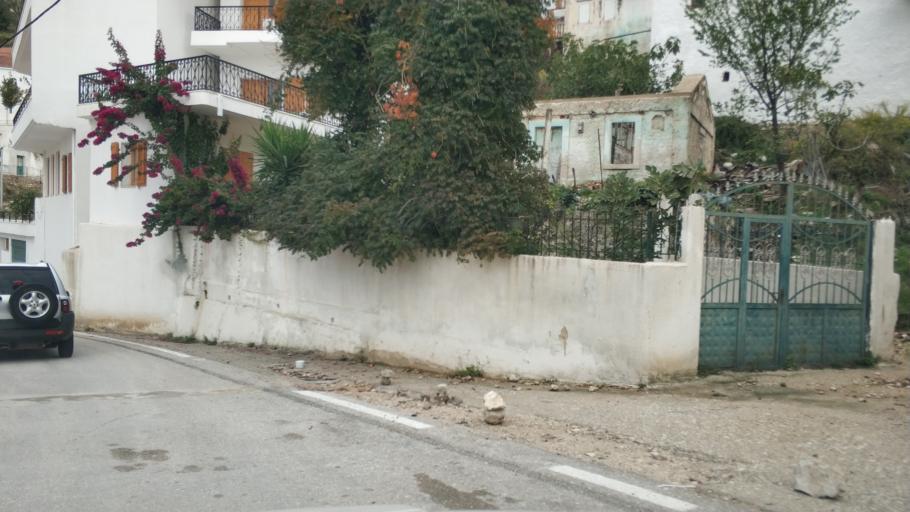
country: AL
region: Vlore
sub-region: Rrethi i Vlores
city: Vranisht
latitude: 40.1530
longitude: 19.6398
